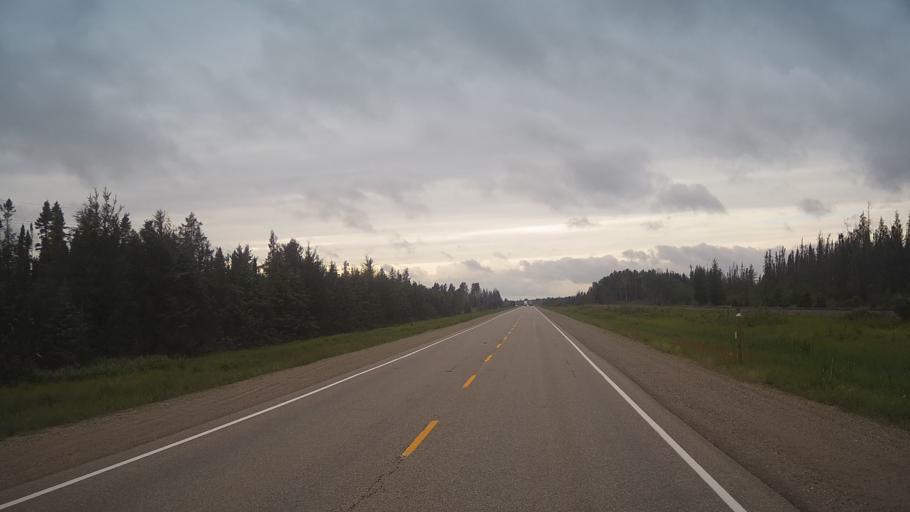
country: CA
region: Ontario
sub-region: Thunder Bay District
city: Thunder Bay
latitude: 48.8647
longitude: -89.9684
